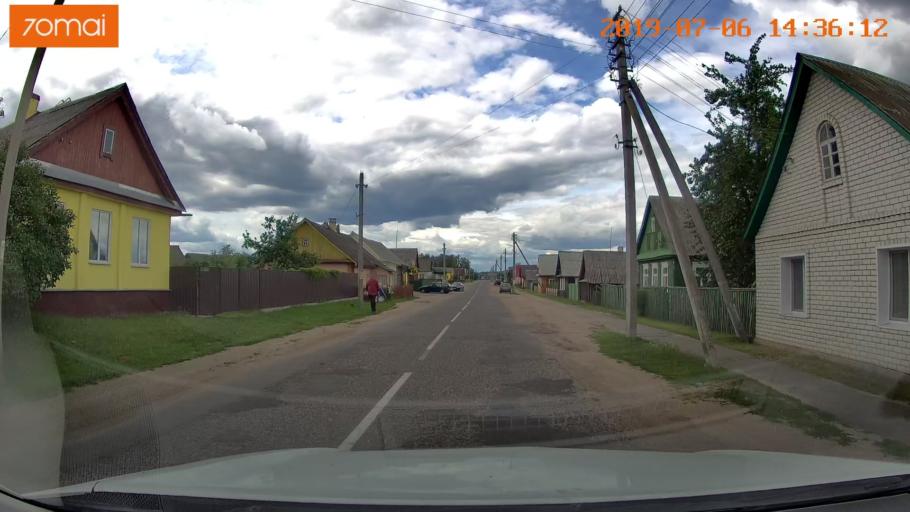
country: BY
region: Minsk
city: Ivyanyets
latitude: 53.8894
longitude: 26.7331
